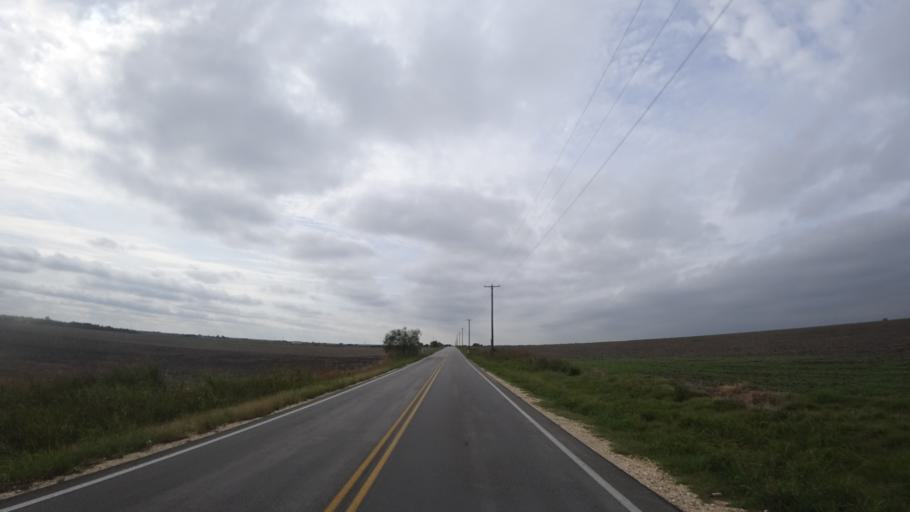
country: US
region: Texas
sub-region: Travis County
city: Manor
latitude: 30.3990
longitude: -97.5466
